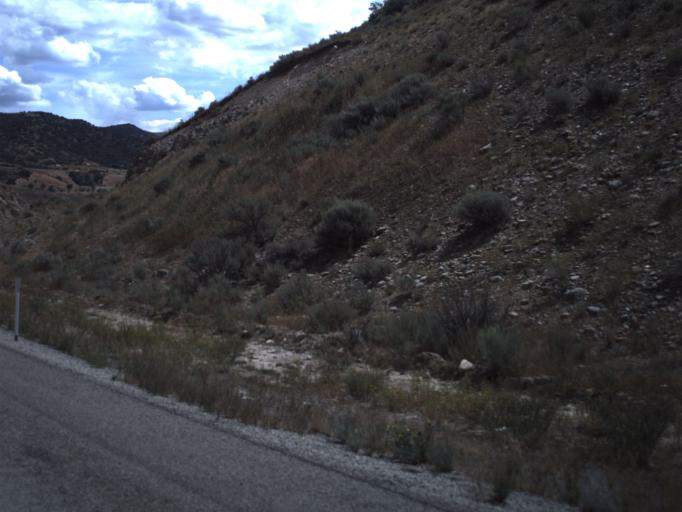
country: US
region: Utah
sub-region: Utah County
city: Woodland Hills
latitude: 39.9932
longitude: -111.4960
